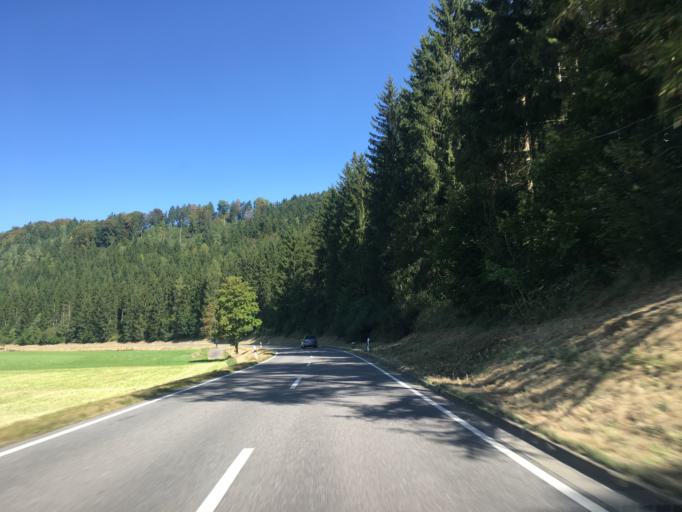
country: DE
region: Baden-Wuerttemberg
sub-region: Tuebingen Region
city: Munsingen
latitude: 48.3498
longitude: 9.4840
